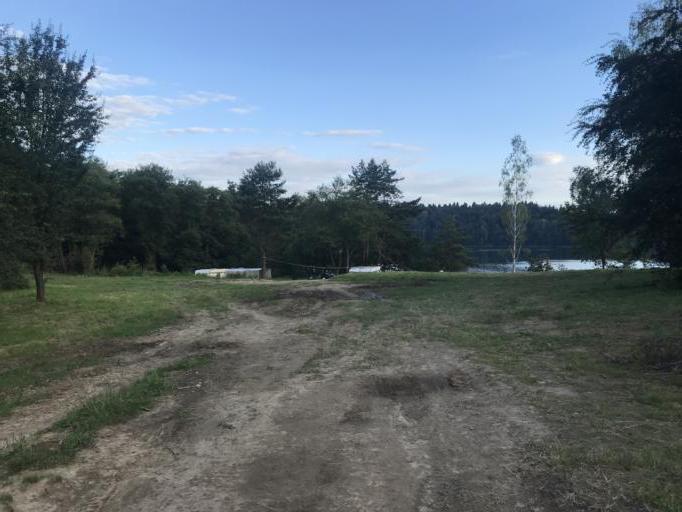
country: PL
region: Subcarpathian Voivodeship
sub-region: Powiat leski
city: Polanczyk
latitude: 49.3593
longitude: 22.4383
